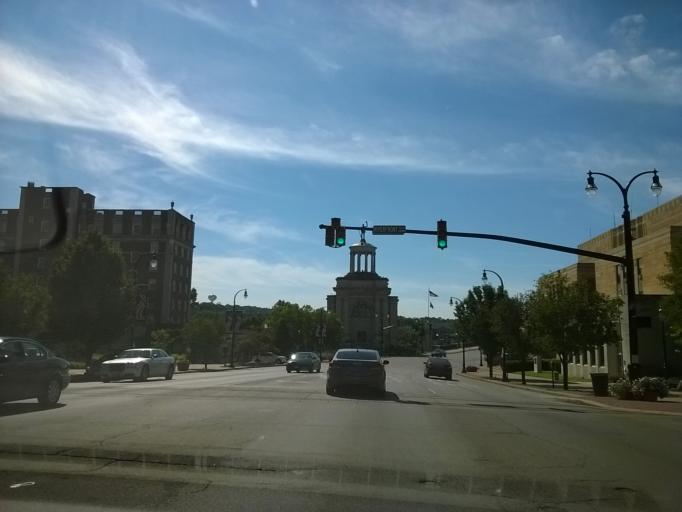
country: US
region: Ohio
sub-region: Butler County
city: Hamilton
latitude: 39.4002
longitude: -84.5633
